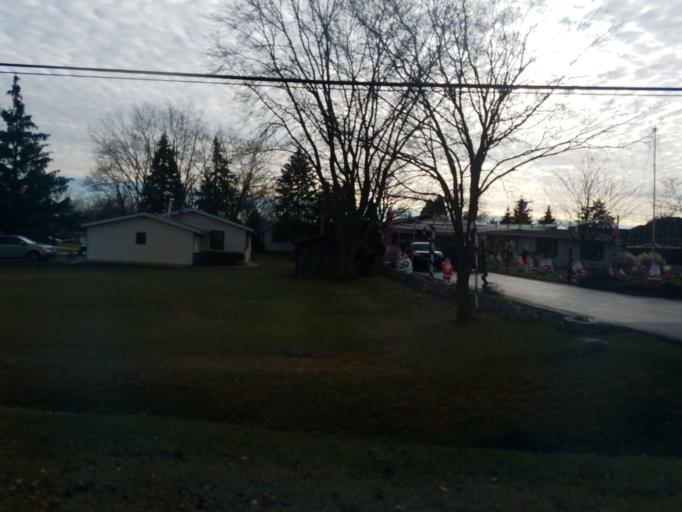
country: US
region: Illinois
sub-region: Will County
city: Mokena
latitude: 41.5274
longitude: -87.9004
